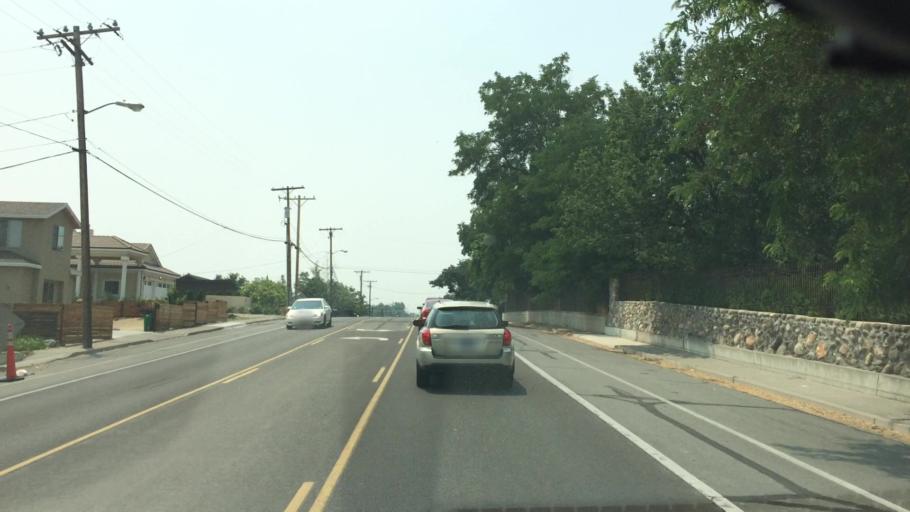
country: US
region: Nevada
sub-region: Washoe County
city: Reno
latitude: 39.5083
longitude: -119.8173
